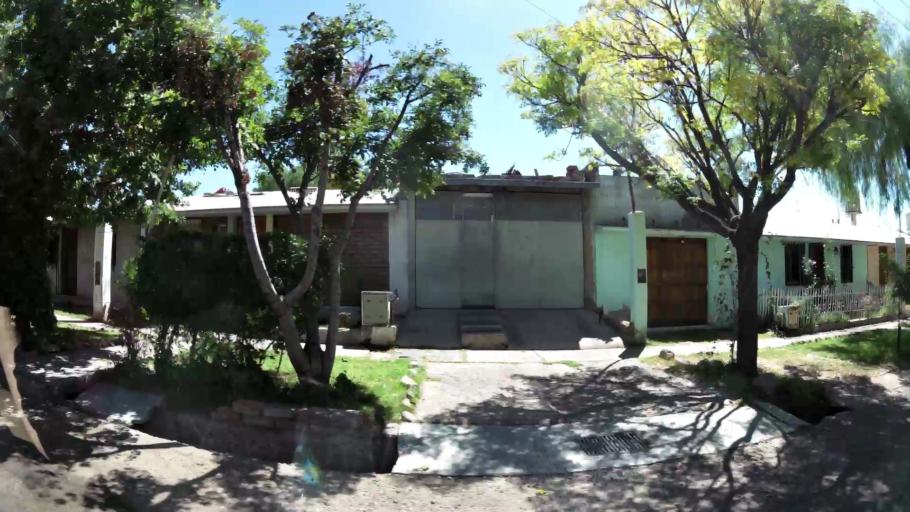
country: AR
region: Mendoza
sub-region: Departamento de Godoy Cruz
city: Godoy Cruz
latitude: -32.9347
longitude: -68.8717
